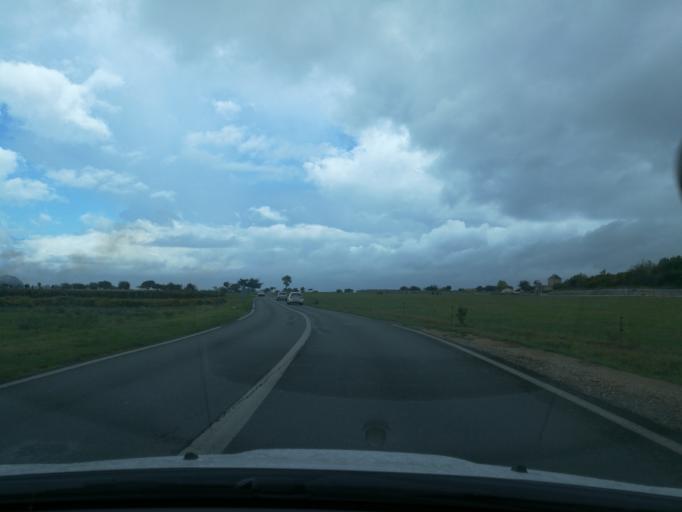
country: FR
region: Poitou-Charentes
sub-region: Departement de la Charente-Maritime
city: Saint-Martin-de-Re
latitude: 46.1984
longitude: -1.3717
